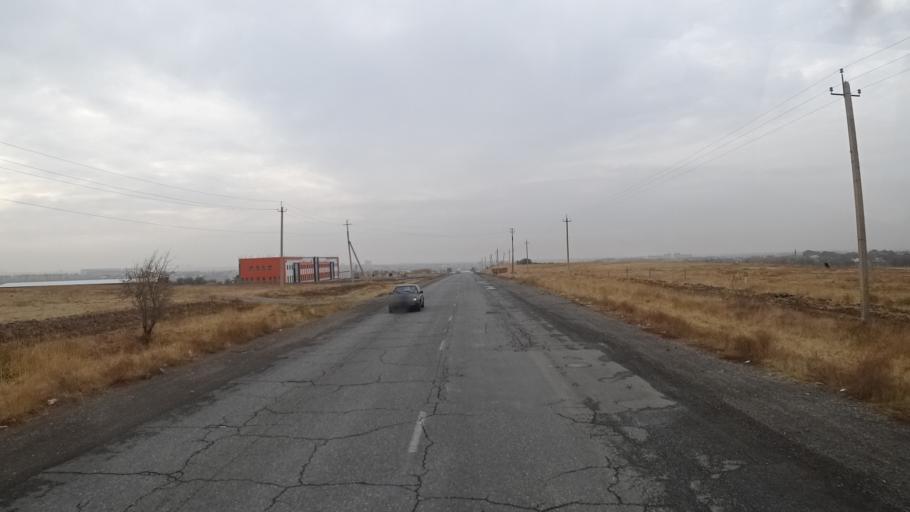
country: KZ
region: Ongtustik Qazaqstan
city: Shymkent
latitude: 42.4138
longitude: 69.6747
